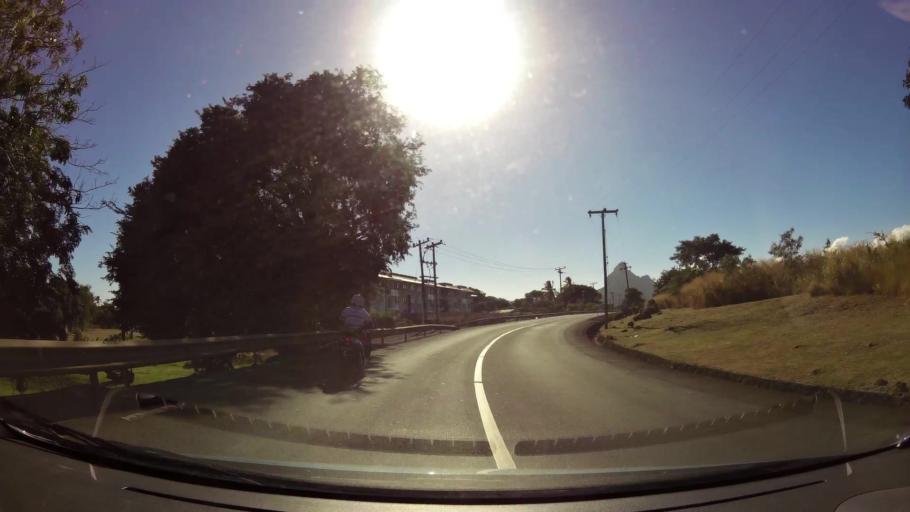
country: MU
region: Black River
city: Tamarin
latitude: -20.3295
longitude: 57.3812
